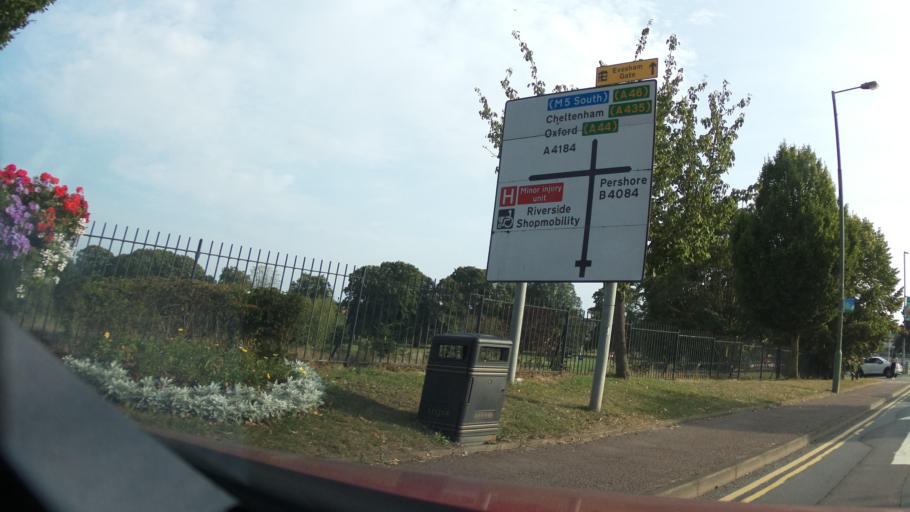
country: GB
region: England
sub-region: Worcestershire
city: Evesham
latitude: 52.0888
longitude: -1.9512
